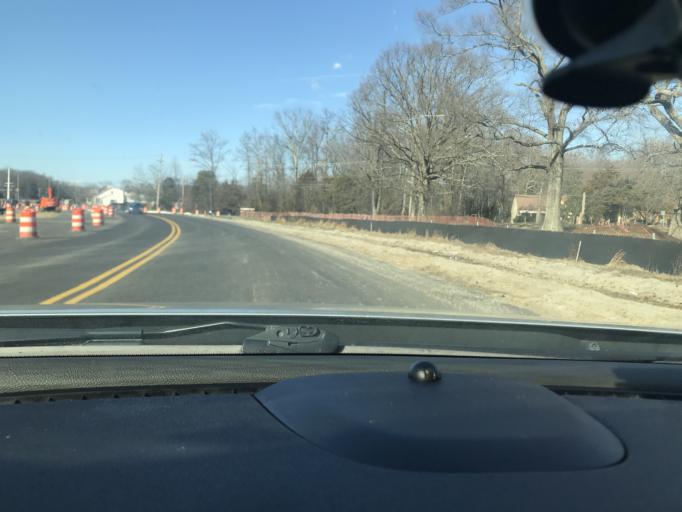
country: US
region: Maryland
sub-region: Prince George's County
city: Brandywine
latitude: 38.7012
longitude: -76.8722
